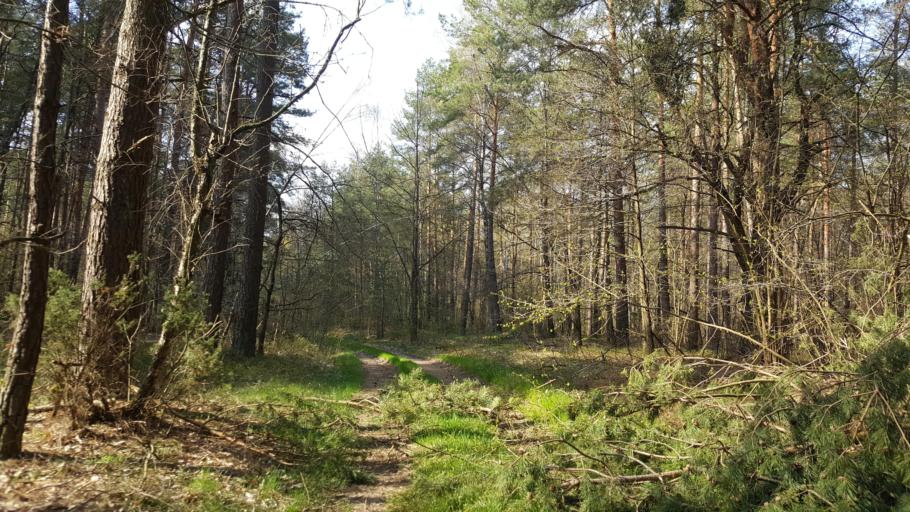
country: BY
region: Brest
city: Kamyanyets
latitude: 52.3454
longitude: 23.8450
